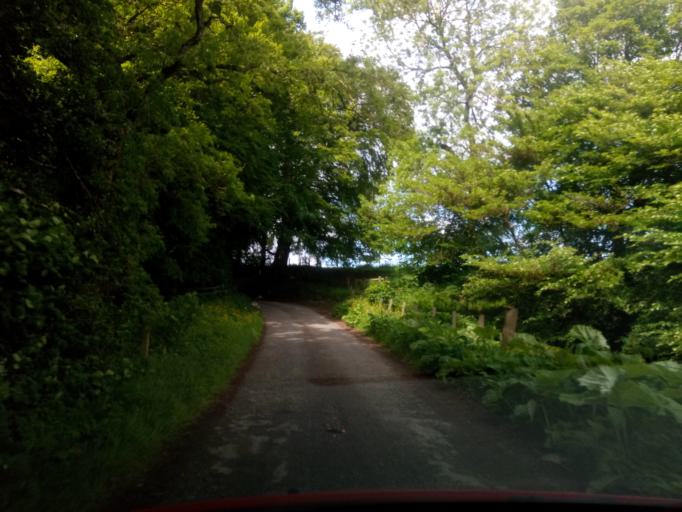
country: GB
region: Scotland
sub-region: The Scottish Borders
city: Selkirk
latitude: 55.5285
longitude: -2.8671
